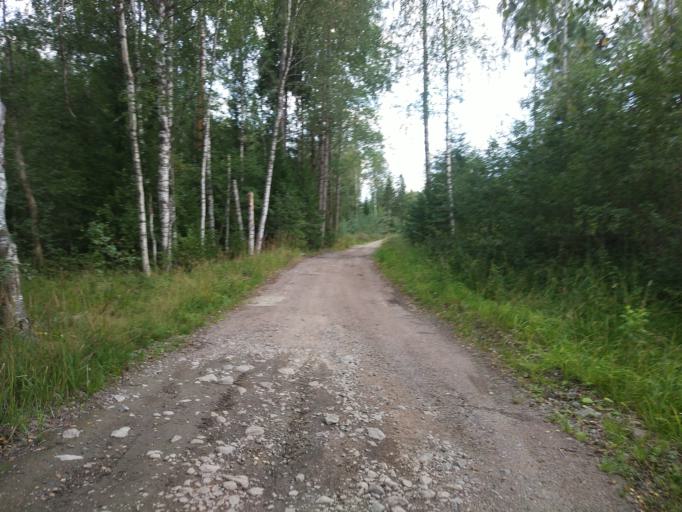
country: RU
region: Leningrad
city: Kuznechnoye
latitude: 61.1111
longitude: 29.6123
